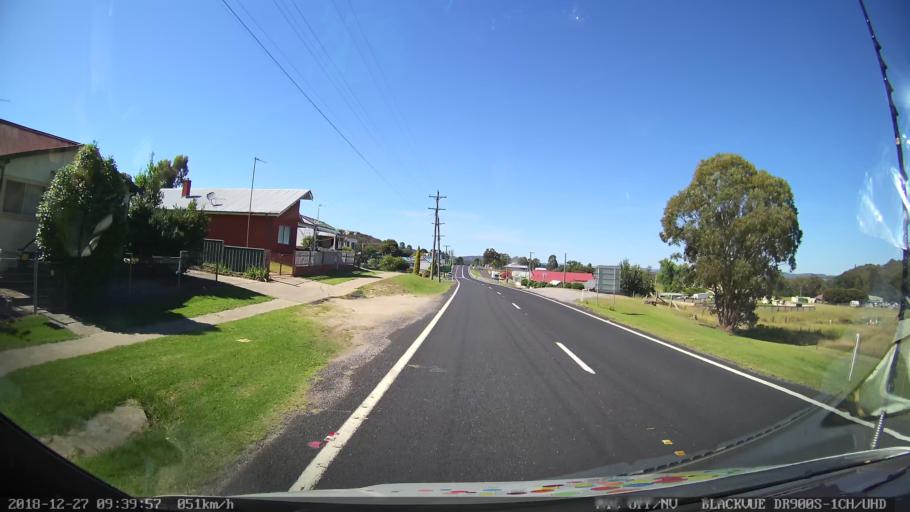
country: AU
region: New South Wales
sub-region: Lithgow
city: Portland
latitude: -33.2971
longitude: 150.0337
